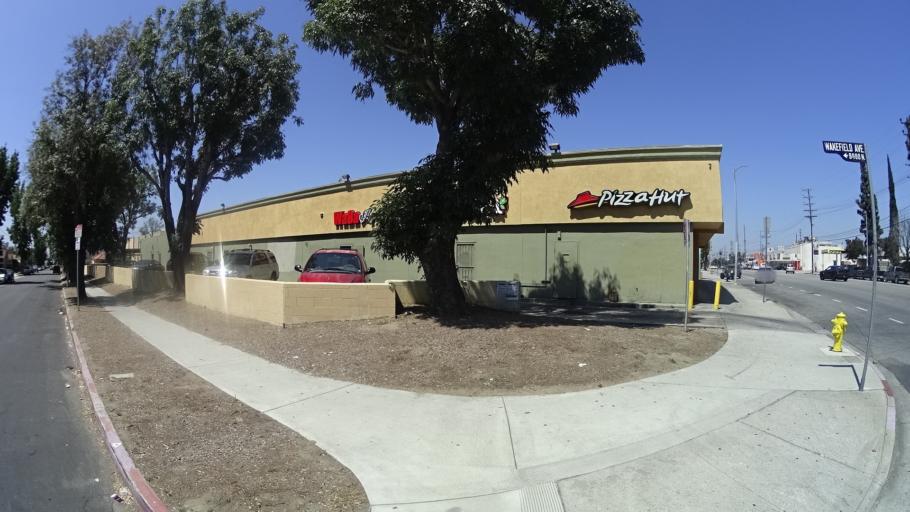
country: US
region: California
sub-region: Los Angeles County
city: San Fernando
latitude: 34.2353
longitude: -118.4481
